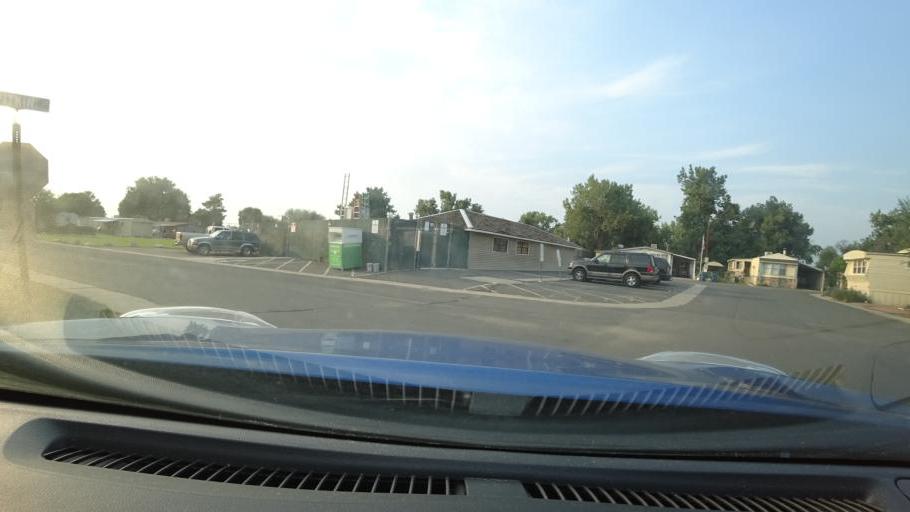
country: US
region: Colorado
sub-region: Adams County
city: Aurora
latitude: 39.7462
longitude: -104.7883
